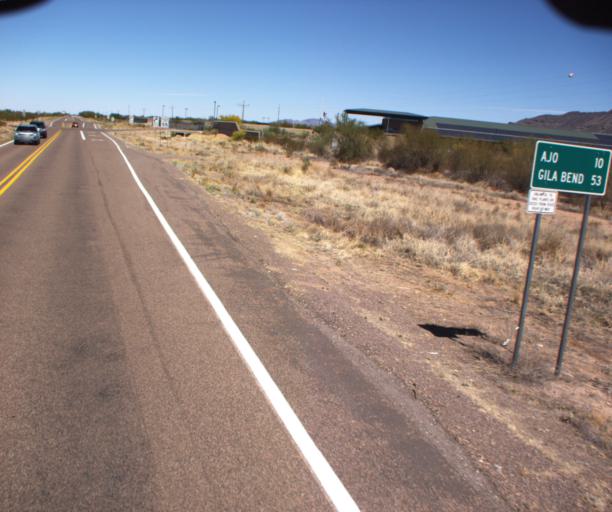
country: US
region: Arizona
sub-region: Pima County
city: Ajo
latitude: 32.2741
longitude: -112.7413
